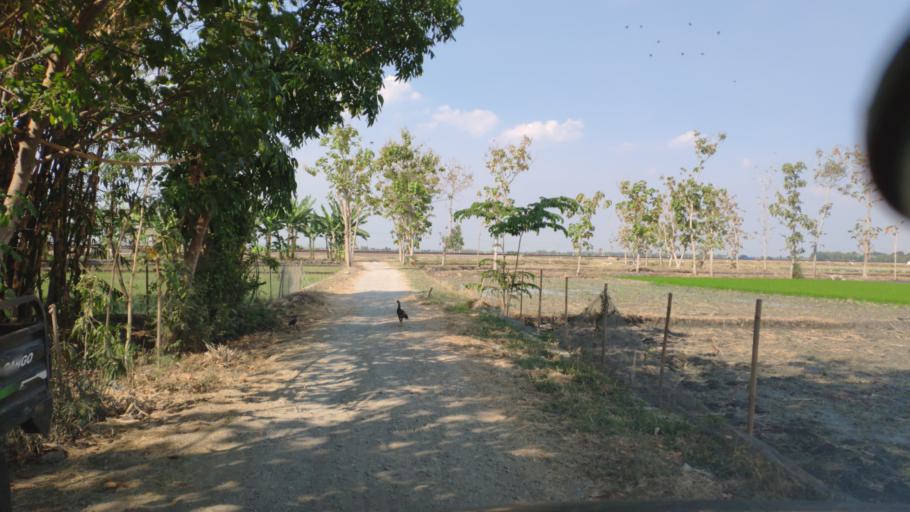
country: ID
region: Central Java
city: Pulo
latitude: -7.1968
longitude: 111.5051
